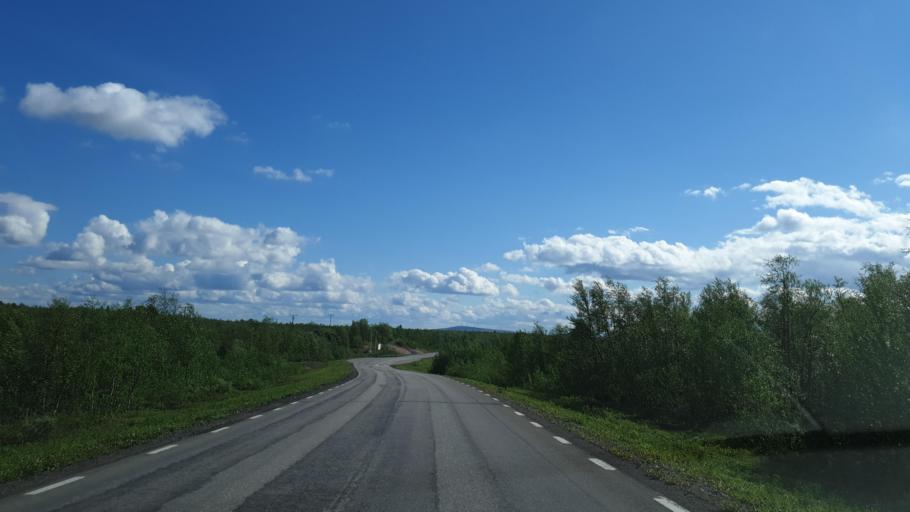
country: SE
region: Norrbotten
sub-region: Kiruna Kommun
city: Kiruna
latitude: 67.7880
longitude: 20.2293
